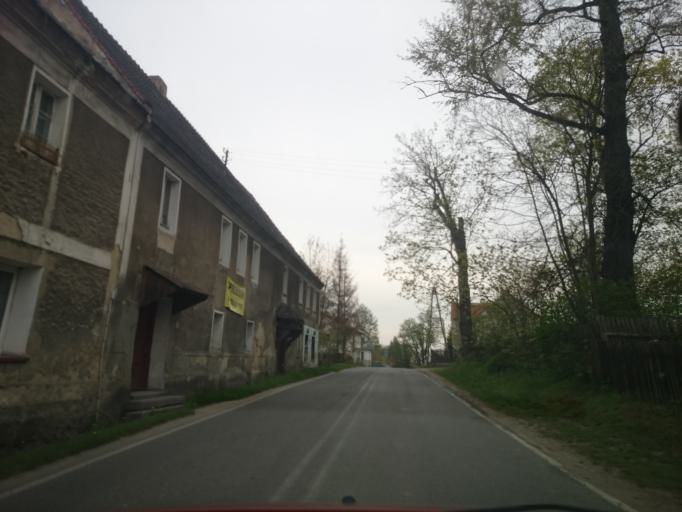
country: PL
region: Lower Silesian Voivodeship
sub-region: Powiat strzelinski
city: Przeworno
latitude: 50.6463
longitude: 17.1717
